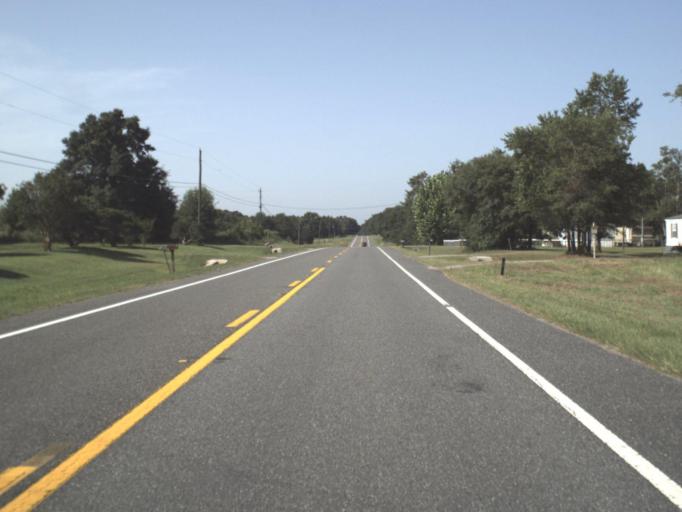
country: US
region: Florida
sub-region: Columbia County
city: Lake City
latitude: 30.0402
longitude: -82.7068
